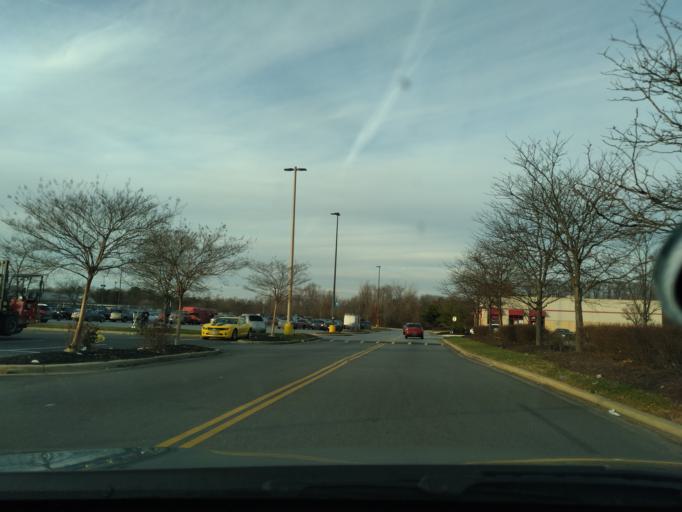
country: US
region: Maryland
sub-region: Prince George's County
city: Clinton
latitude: 38.7709
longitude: -76.8875
